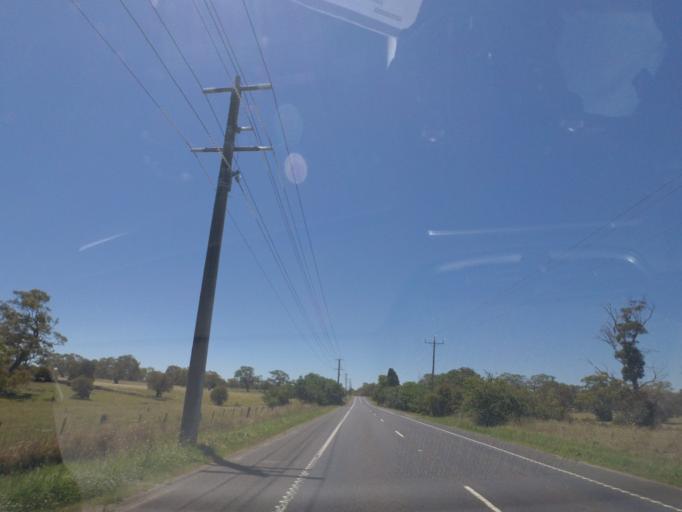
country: AU
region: Victoria
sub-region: Whittlesea
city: Mernda
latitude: -37.5676
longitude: 145.0325
